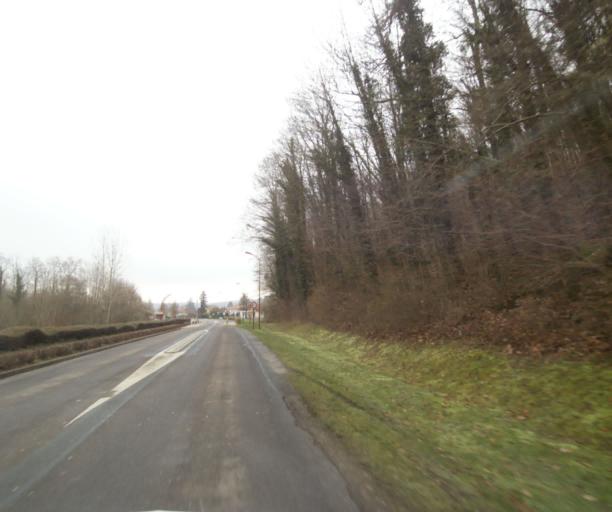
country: FR
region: Champagne-Ardenne
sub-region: Departement de la Haute-Marne
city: Bienville
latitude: 48.5469
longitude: 5.0768
